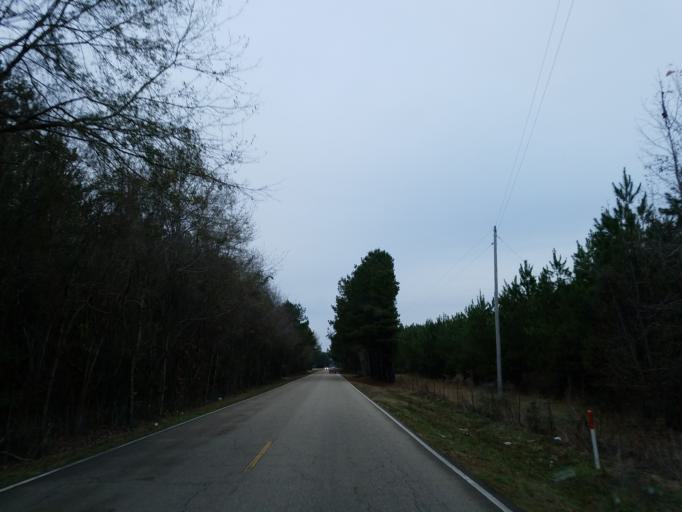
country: US
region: Mississippi
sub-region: Forrest County
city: Hattiesburg
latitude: 31.2624
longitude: -89.2379
